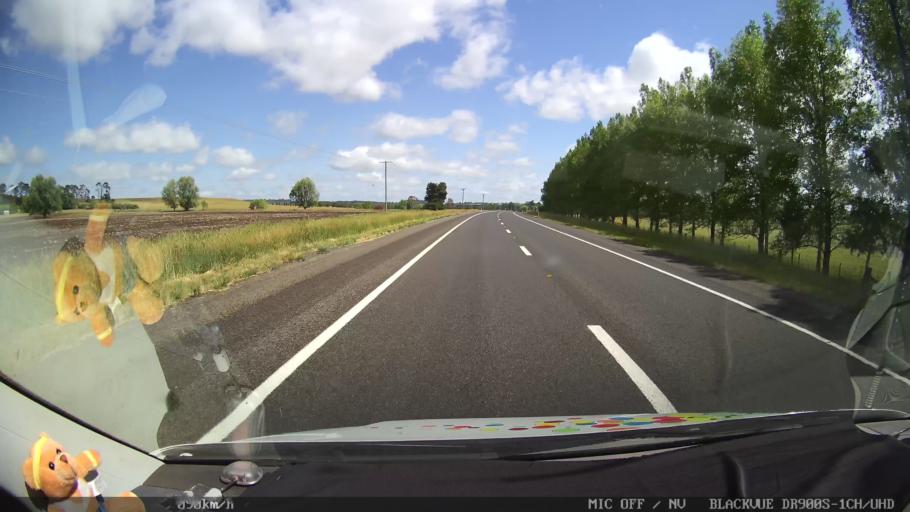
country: AU
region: New South Wales
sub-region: Glen Innes Severn
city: Glen Innes
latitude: -29.8347
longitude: 151.7376
